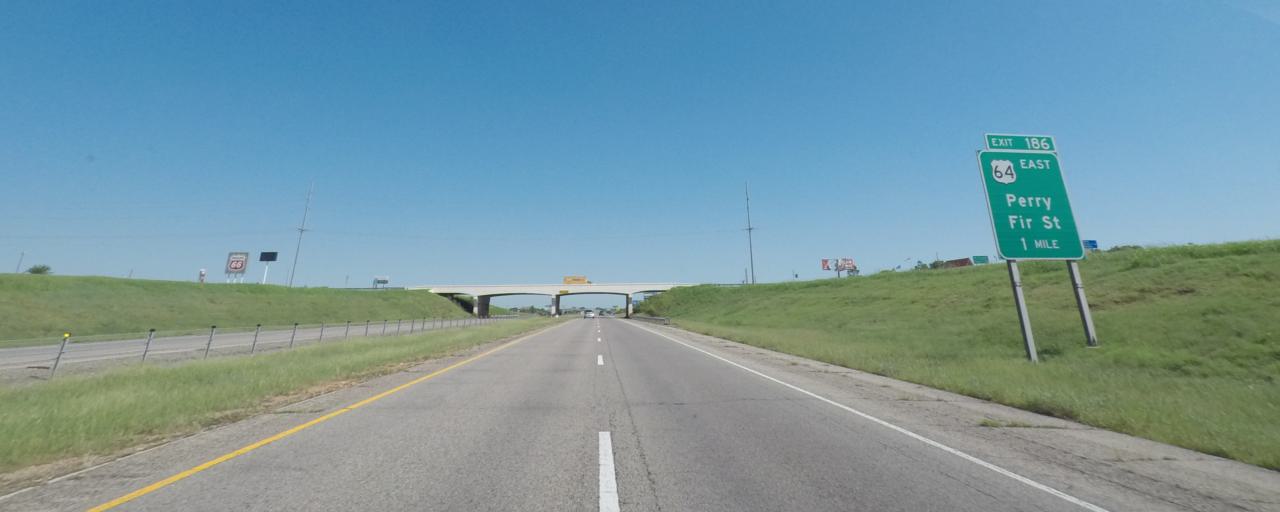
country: US
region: Oklahoma
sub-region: Noble County
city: Perry
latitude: 36.2736
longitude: -97.3276
